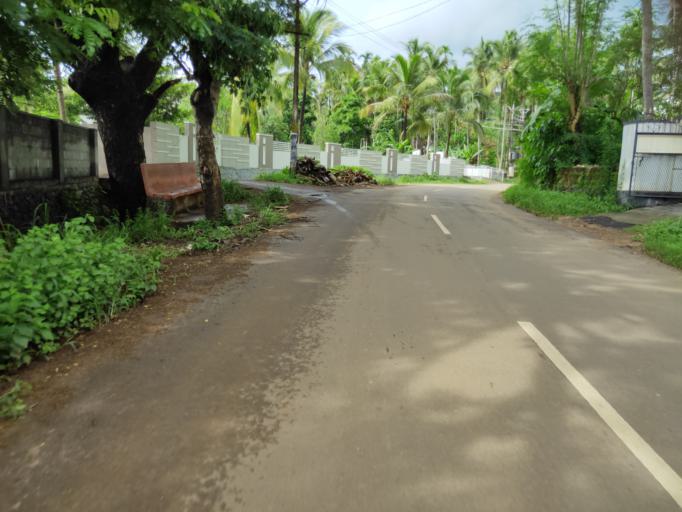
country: IN
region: Kerala
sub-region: Malappuram
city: Manjeri
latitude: 11.1351
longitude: 76.1283
